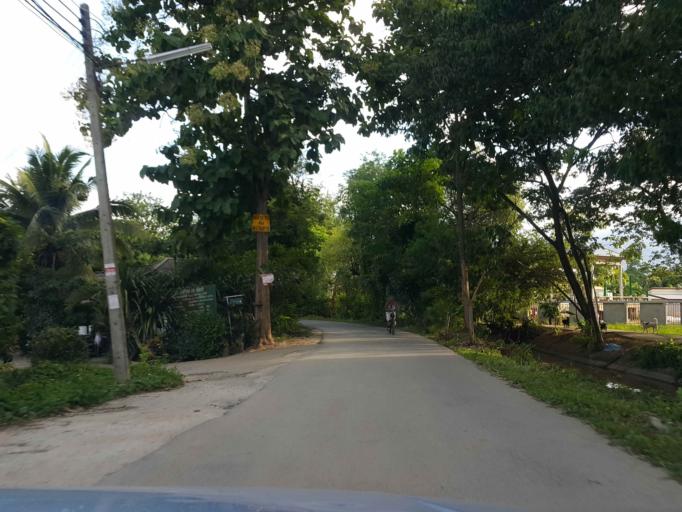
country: TH
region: Chiang Mai
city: San Sai
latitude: 18.9074
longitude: 98.9791
